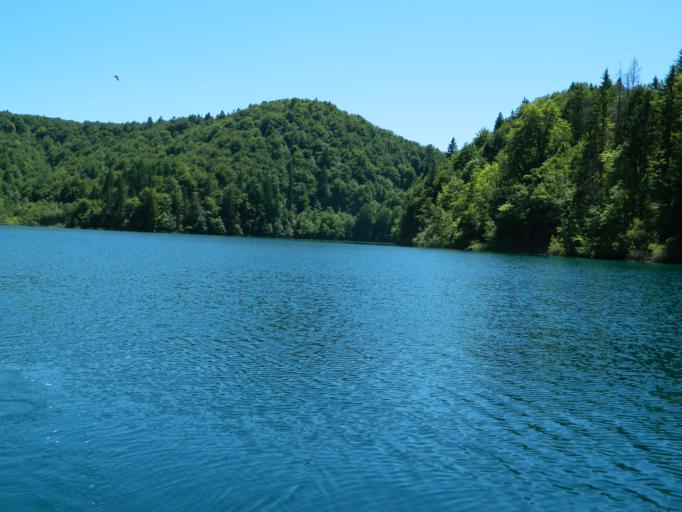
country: HR
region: Licko-Senjska
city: Jezerce
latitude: 44.8803
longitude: 15.6170
